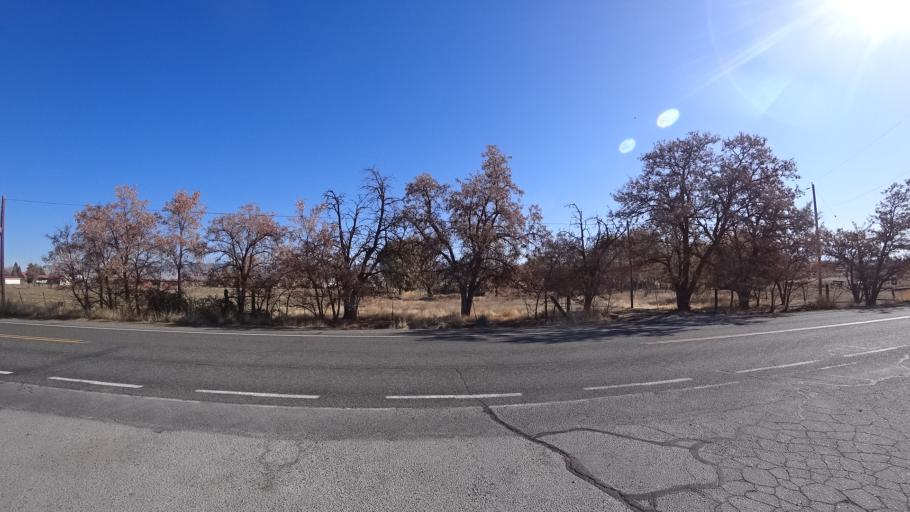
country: US
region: California
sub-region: Siskiyou County
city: Montague
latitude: 41.7419
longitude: -122.5247
